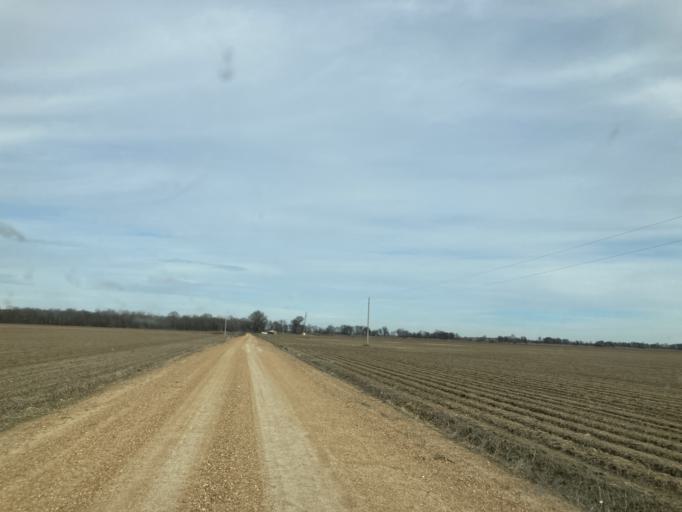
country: US
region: Mississippi
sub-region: Humphreys County
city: Belzoni
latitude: 33.0608
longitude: -90.6577
